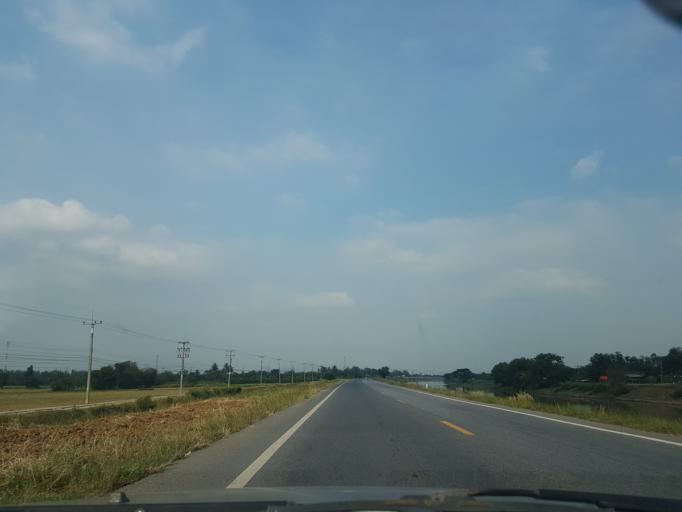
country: TH
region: Phra Nakhon Si Ayutthaya
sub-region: Amphoe Tha Ruea
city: Tha Ruea
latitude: 14.5242
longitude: 100.7401
